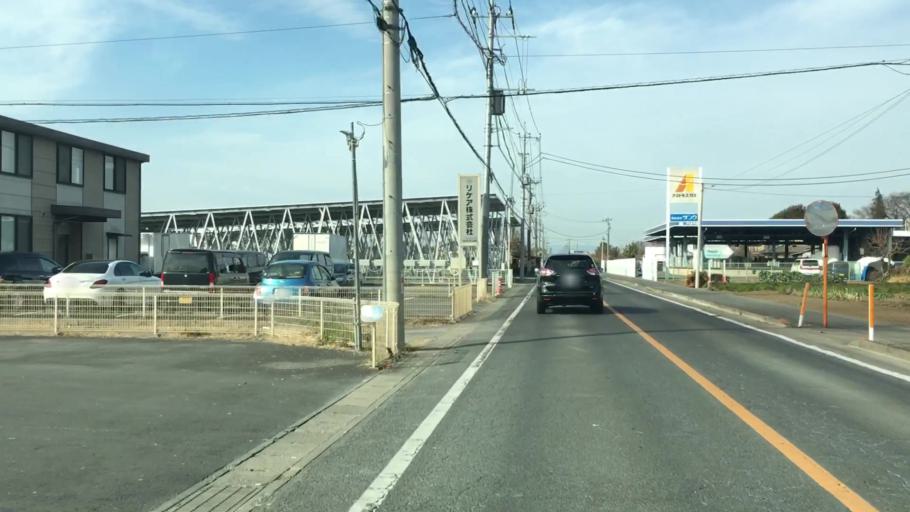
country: JP
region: Saitama
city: Menuma
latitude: 36.2421
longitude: 139.4505
